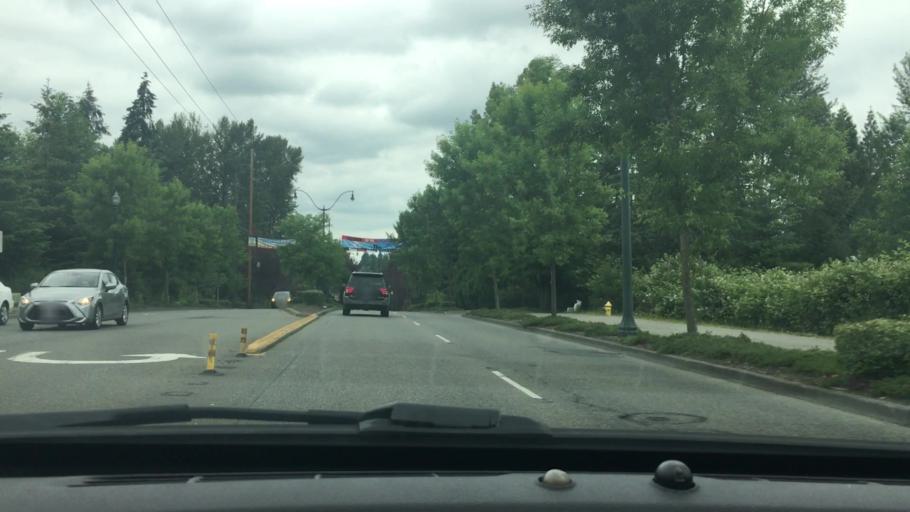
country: US
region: Washington
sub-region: King County
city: City of Sammamish
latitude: 47.6067
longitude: -122.0354
